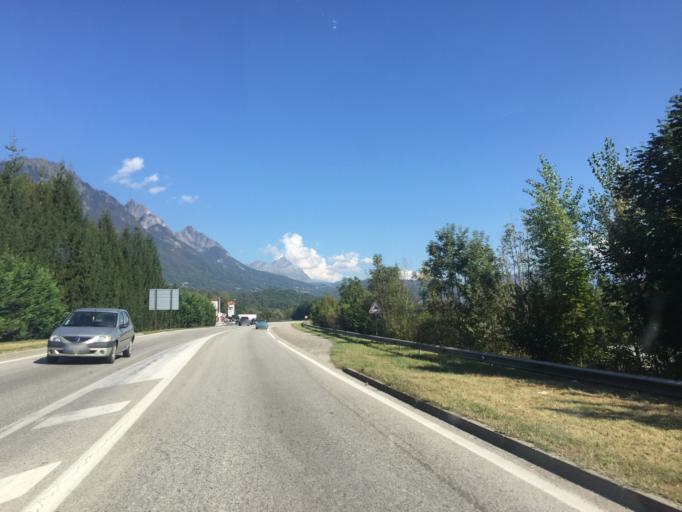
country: FR
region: Rhone-Alpes
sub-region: Departement de la Savoie
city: Frontenex
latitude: 45.6413
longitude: 6.3312
